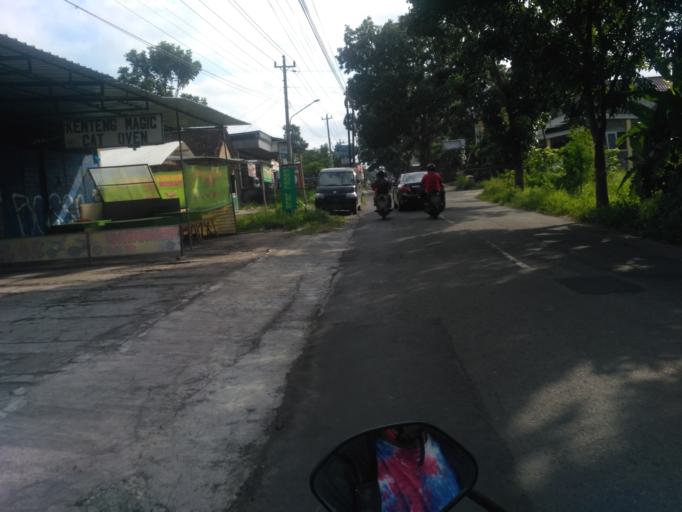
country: ID
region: Daerah Istimewa Yogyakarta
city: Yogyakarta
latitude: -7.7562
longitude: 110.3465
